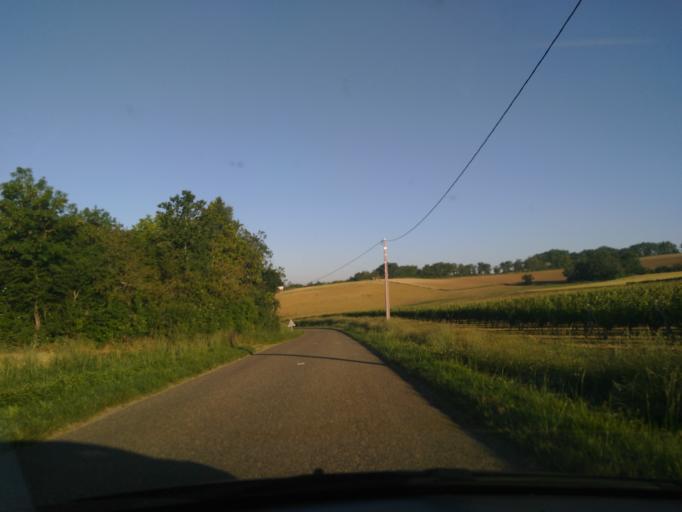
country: FR
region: Midi-Pyrenees
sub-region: Departement du Gers
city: Valence-sur-Baise
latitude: 43.8779
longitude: 0.4113
